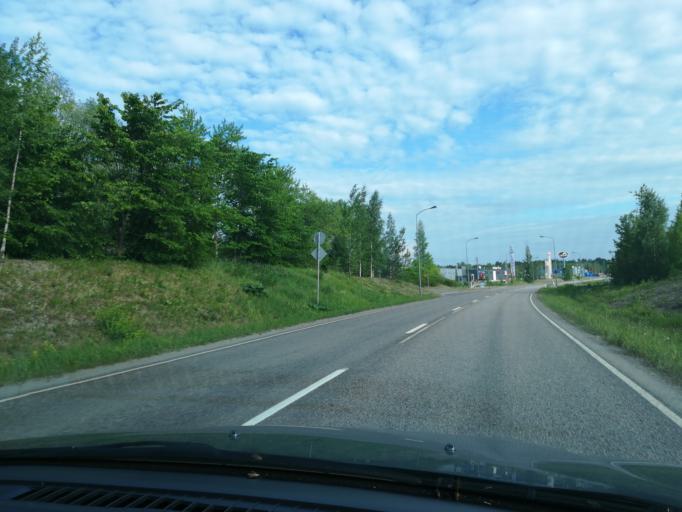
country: FI
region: South Karelia
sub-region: Imatra
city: Imatra
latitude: 61.1526
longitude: 28.8066
